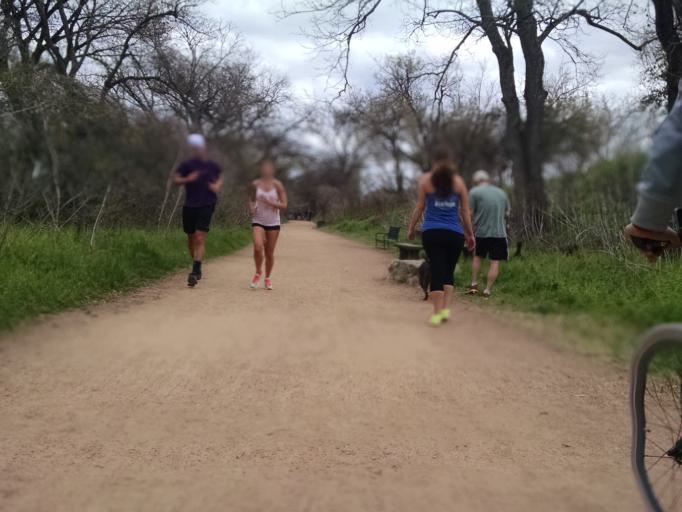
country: US
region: Texas
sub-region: Travis County
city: Austin
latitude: 30.2688
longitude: -97.7655
